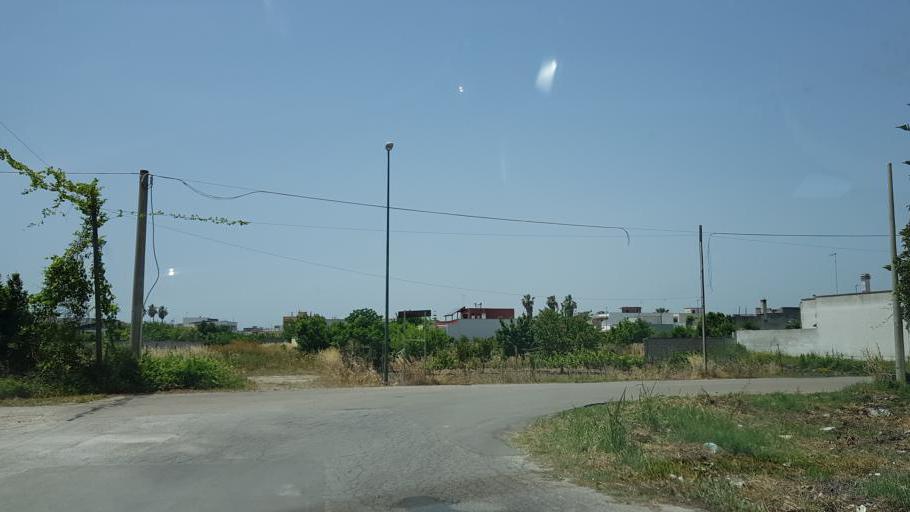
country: IT
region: Apulia
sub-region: Provincia di Brindisi
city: San Pancrazio Salentino
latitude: 40.4227
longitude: 17.8450
